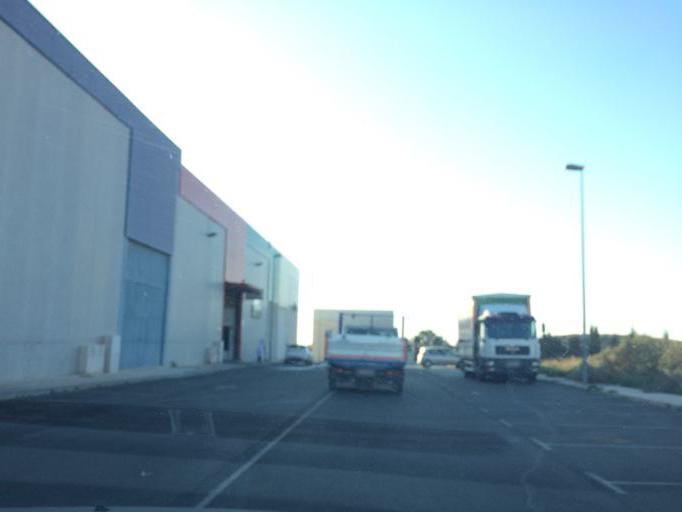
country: ES
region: Andalusia
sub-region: Provincia de Almeria
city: Viator
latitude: 36.8763
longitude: -2.4127
